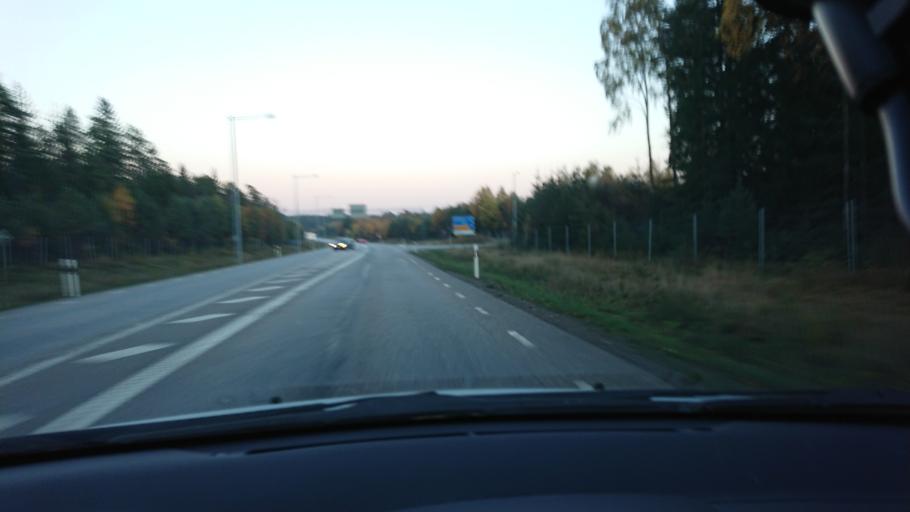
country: SE
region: Halland
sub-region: Laholms Kommun
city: Knared
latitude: 56.7395
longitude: 13.4591
